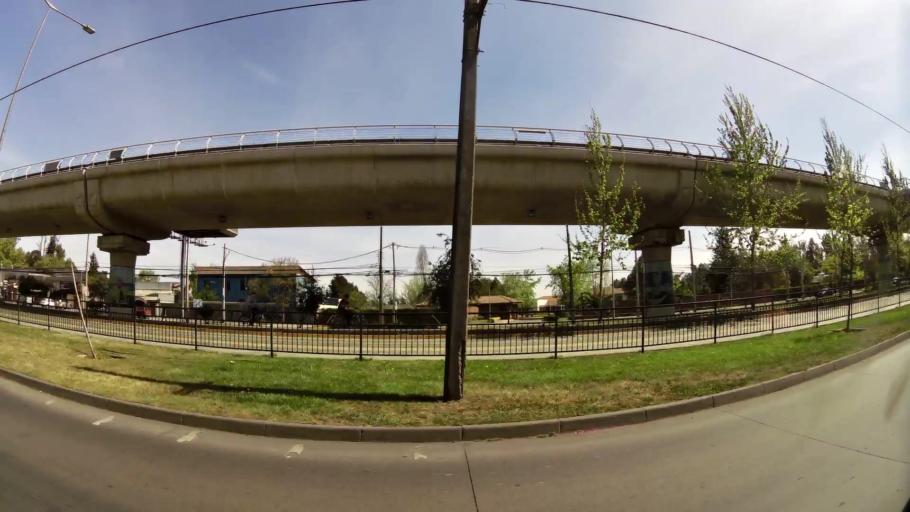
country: CL
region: Santiago Metropolitan
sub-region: Provincia de Cordillera
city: Puente Alto
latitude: -33.5781
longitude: -70.5819
